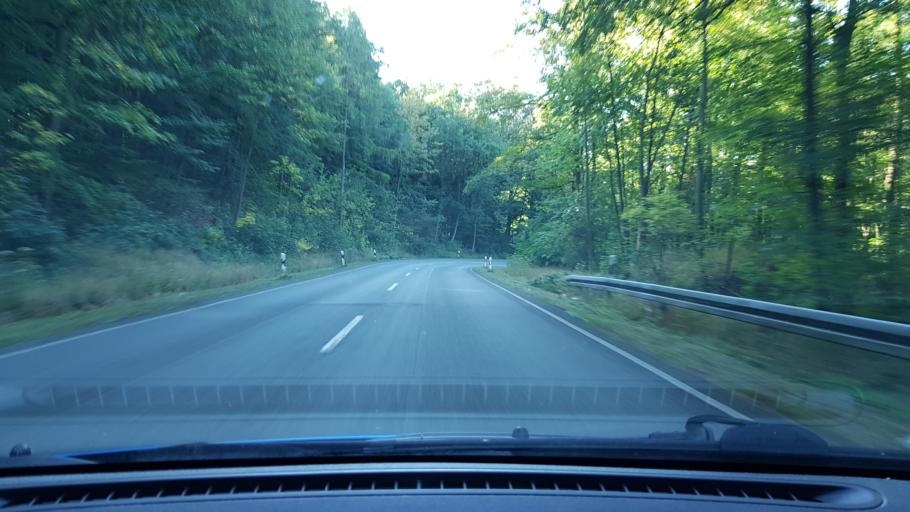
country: DE
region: Lower Saxony
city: Barsinghausen
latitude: 52.2607
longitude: 9.4664
